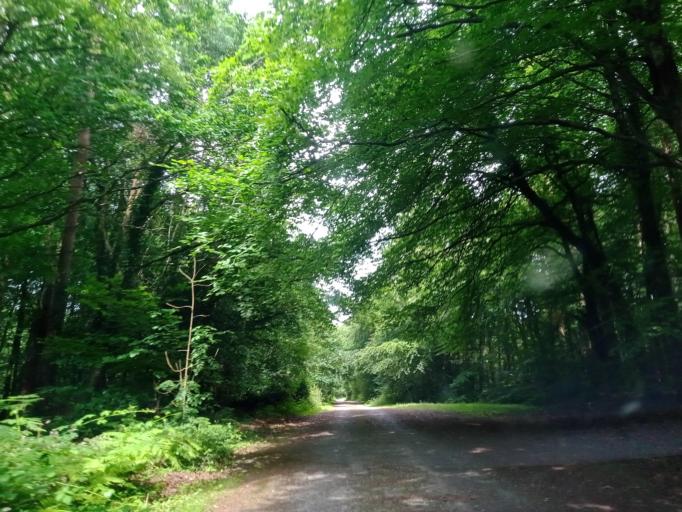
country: IE
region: Leinster
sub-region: Kilkenny
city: Thomastown
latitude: 52.5501
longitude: -7.0883
